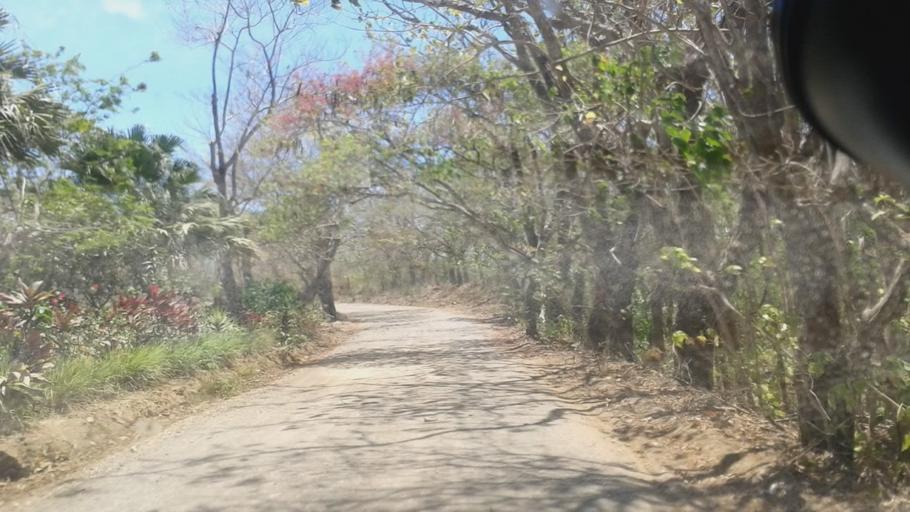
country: CR
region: Guanacaste
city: Samara
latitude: 10.0243
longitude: -85.7135
